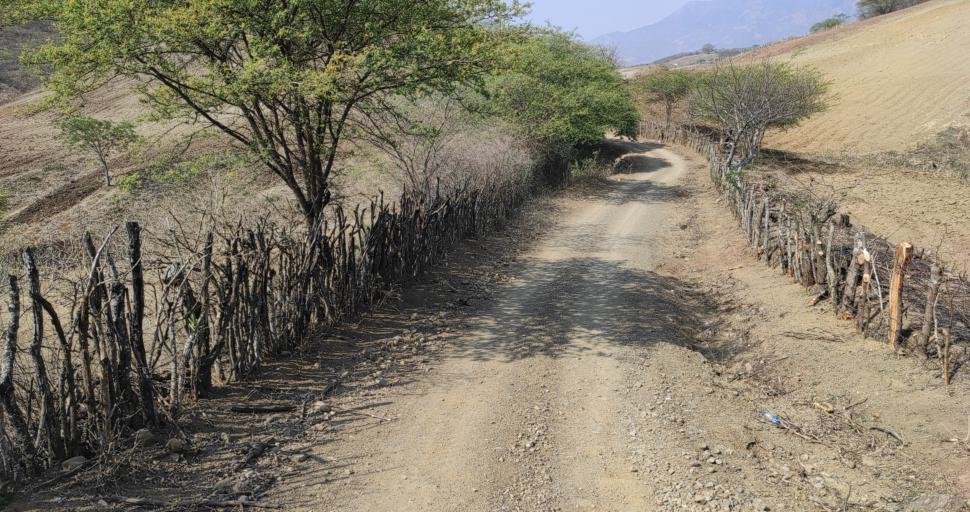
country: EC
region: Loja
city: Catacocha
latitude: -4.0096
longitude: -79.7009
